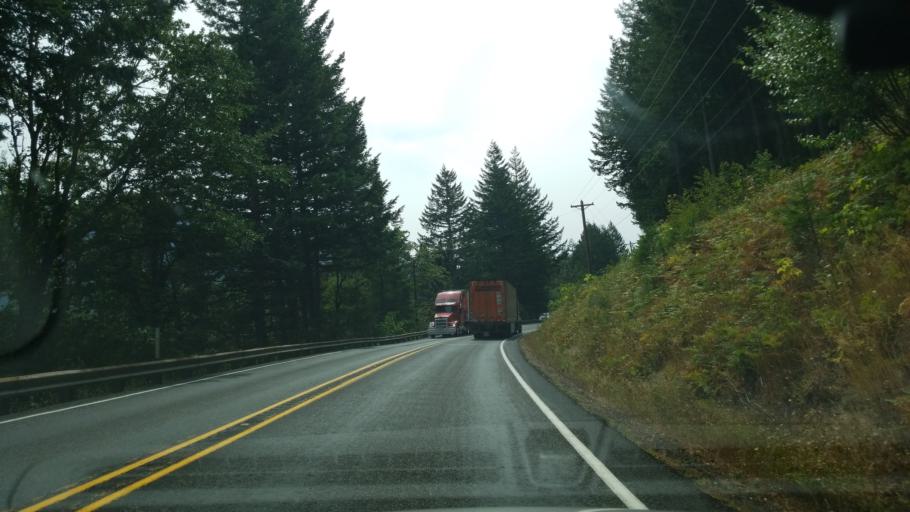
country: US
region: Oregon
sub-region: Hood River County
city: Cascade Locks
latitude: 45.6322
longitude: -122.0064
